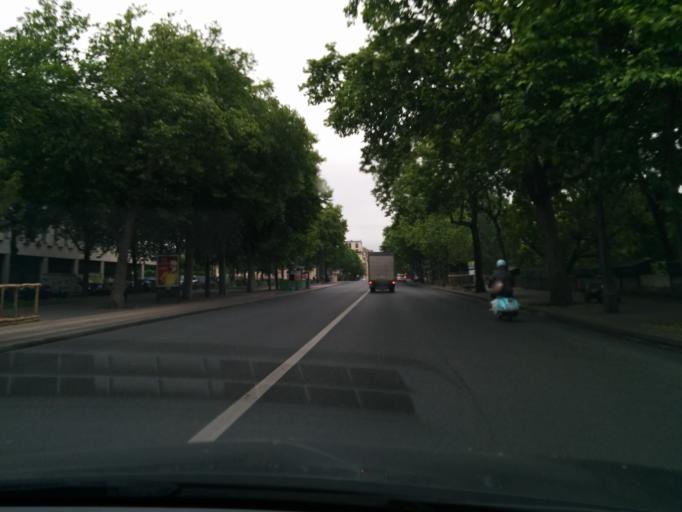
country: FR
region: Ile-de-France
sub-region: Paris
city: Paris
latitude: 48.8540
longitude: 2.3559
